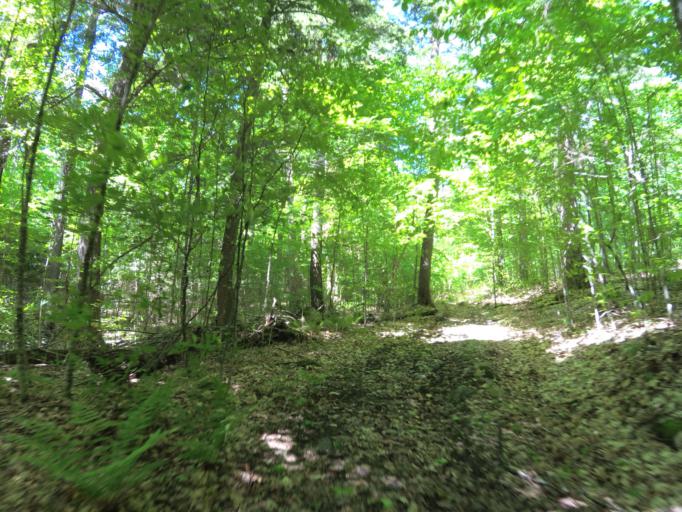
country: CA
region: Ontario
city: Renfrew
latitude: 45.0583
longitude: -76.8440
